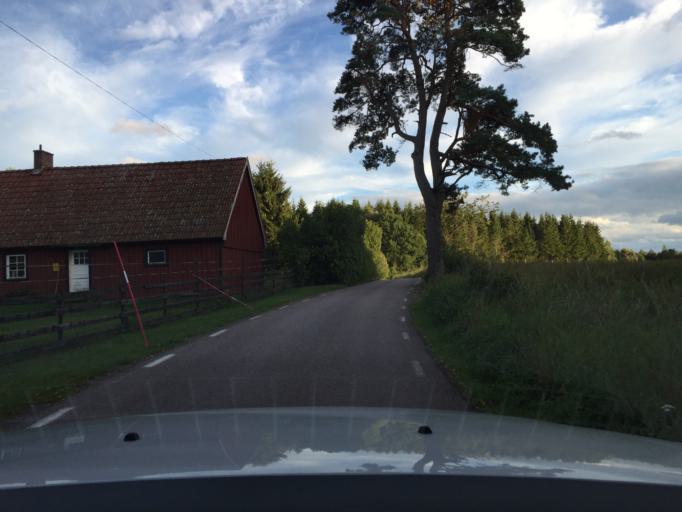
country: SE
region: Skane
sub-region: Hassleholms Kommun
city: Tormestorp
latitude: 56.0209
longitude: 13.7750
